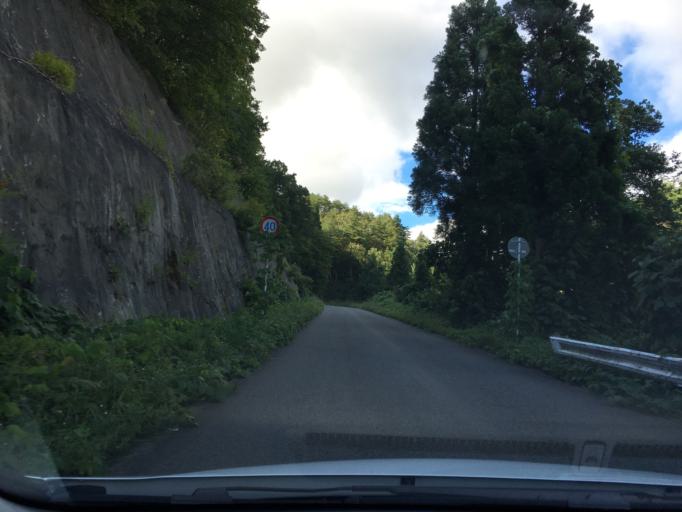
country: JP
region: Yamagata
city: Yonezawa
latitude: 37.8967
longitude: 140.2003
